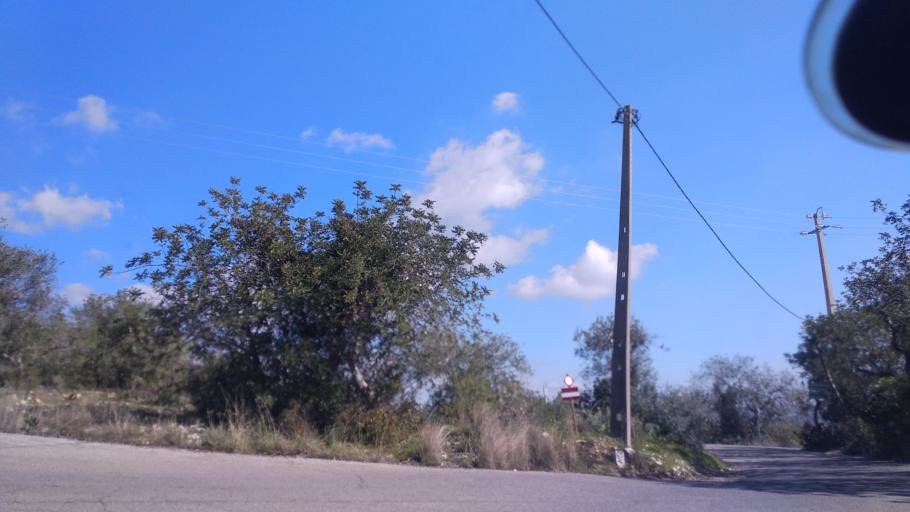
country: PT
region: Faro
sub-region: Sao Bras de Alportel
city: Sao Bras de Alportel
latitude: 37.1342
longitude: -7.9064
